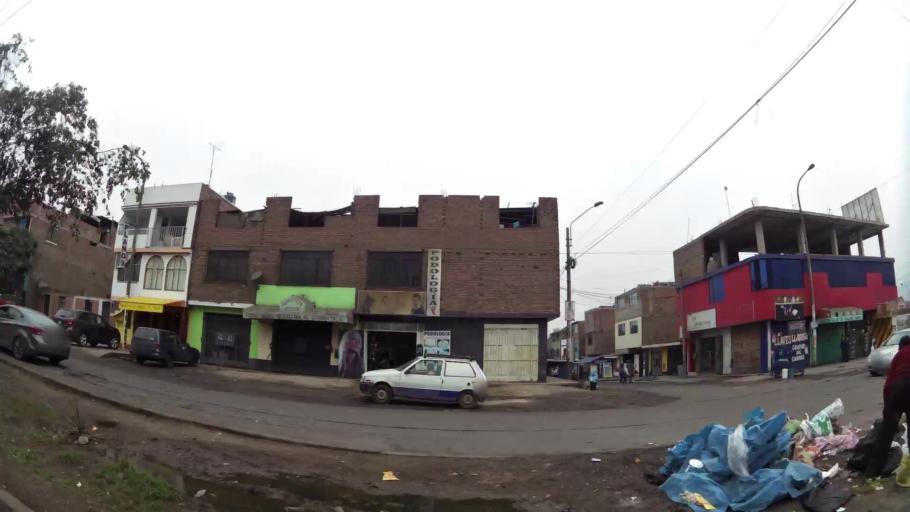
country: PE
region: Lima
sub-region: Lima
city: Independencia
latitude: -11.9439
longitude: -76.9813
